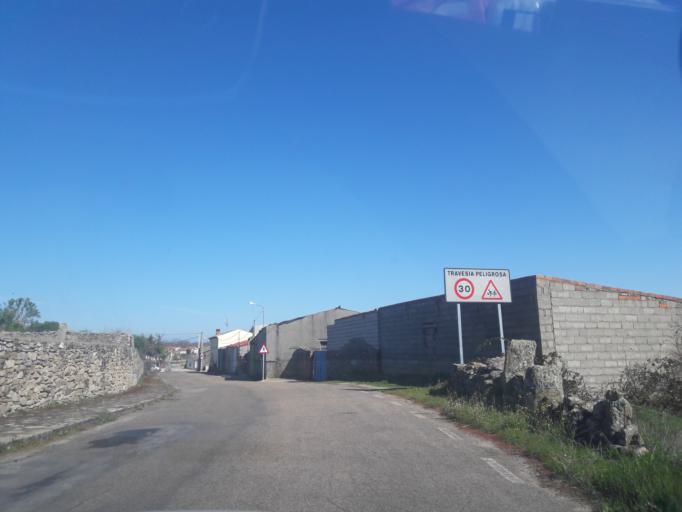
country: ES
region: Castille and Leon
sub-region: Provincia de Salamanca
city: Valsalabroso
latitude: 41.1510
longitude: -6.4865
